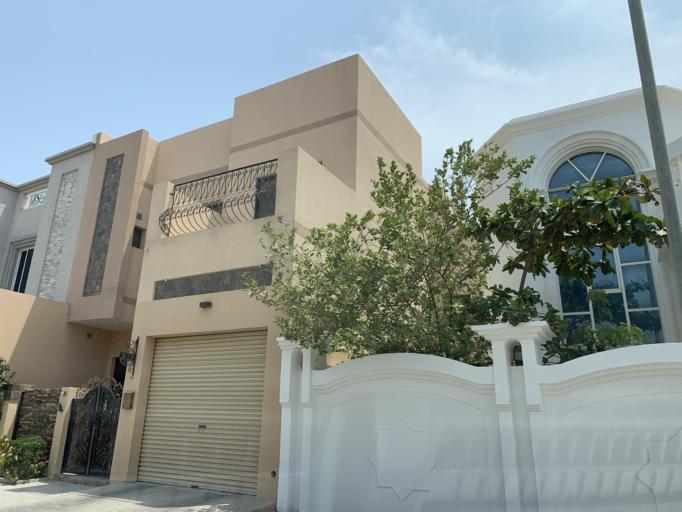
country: BH
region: Muharraq
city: Al Hadd
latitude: 26.2775
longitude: 50.6454
